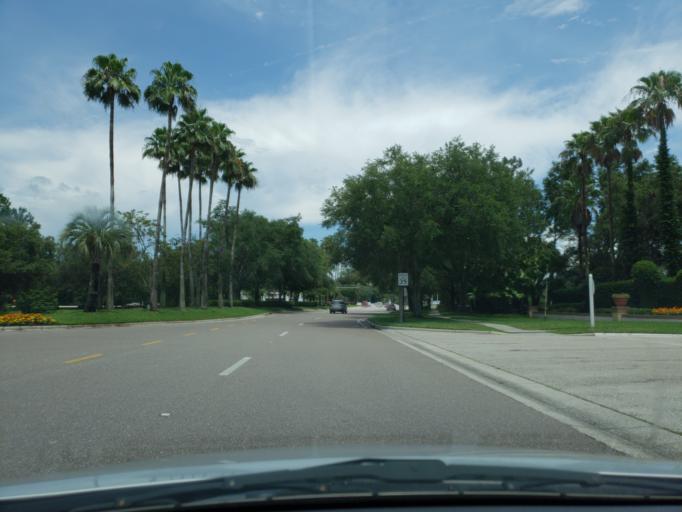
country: US
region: Florida
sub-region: Hillsborough County
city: Pebble Creek
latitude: 28.1172
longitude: -82.3819
